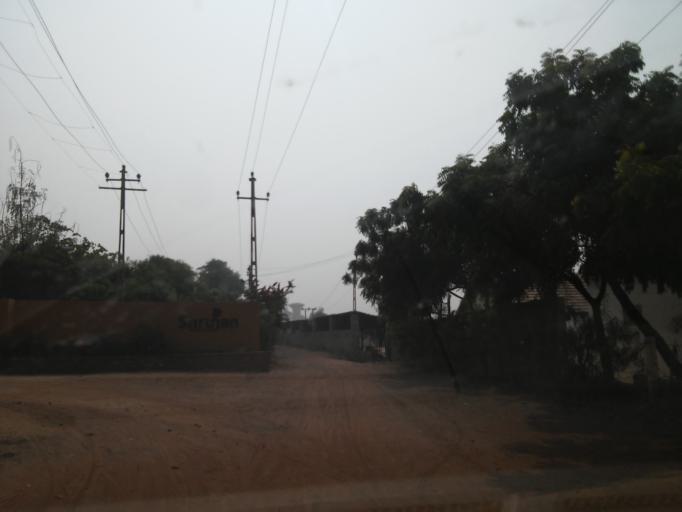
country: IN
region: Gujarat
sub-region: Kachchh
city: Bhuj
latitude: 23.2305
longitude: 69.7402
